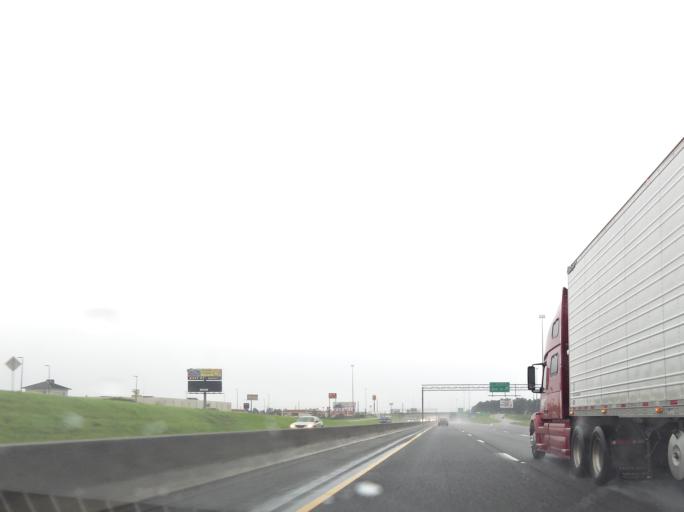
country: US
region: Georgia
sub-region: Tift County
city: Tifton
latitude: 31.4629
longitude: -83.5300
